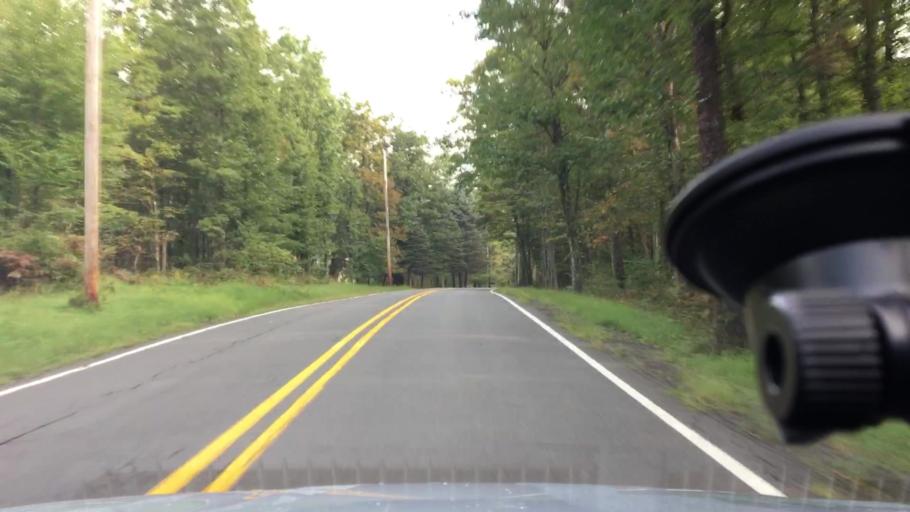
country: US
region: Pennsylvania
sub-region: Monroe County
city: Mountainhome
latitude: 41.1400
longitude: -75.2600
